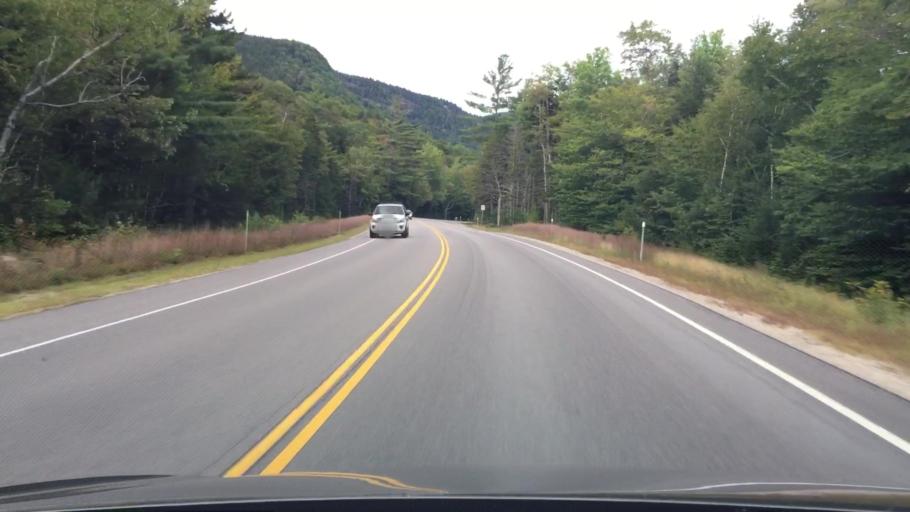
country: US
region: New Hampshire
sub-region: Carroll County
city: North Conway
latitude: 44.0093
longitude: -71.2695
